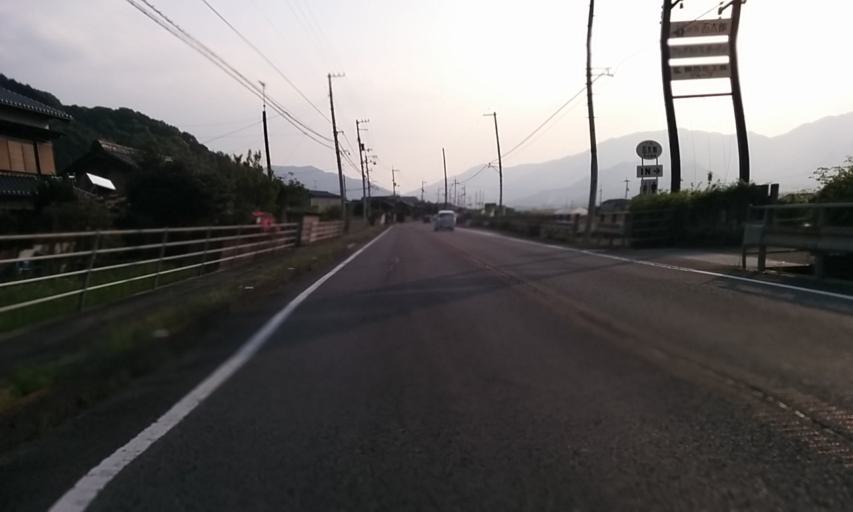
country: JP
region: Ehime
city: Saijo
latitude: 33.8786
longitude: 133.0694
